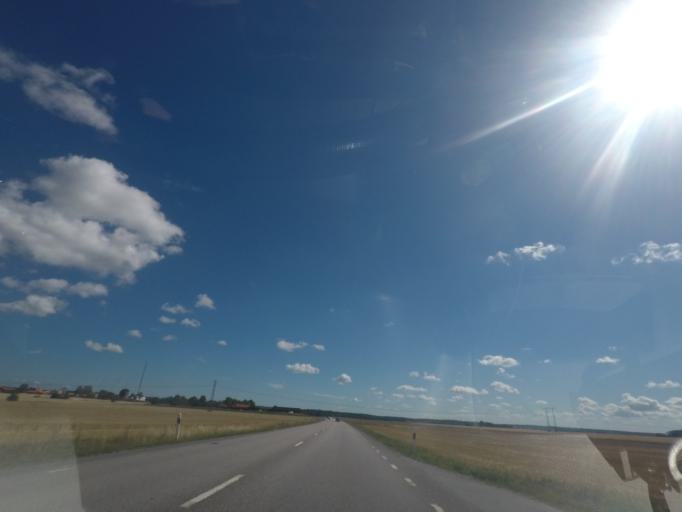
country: SE
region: Uppsala
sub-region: Uppsala Kommun
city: Saevja
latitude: 59.8443
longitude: 17.7416
